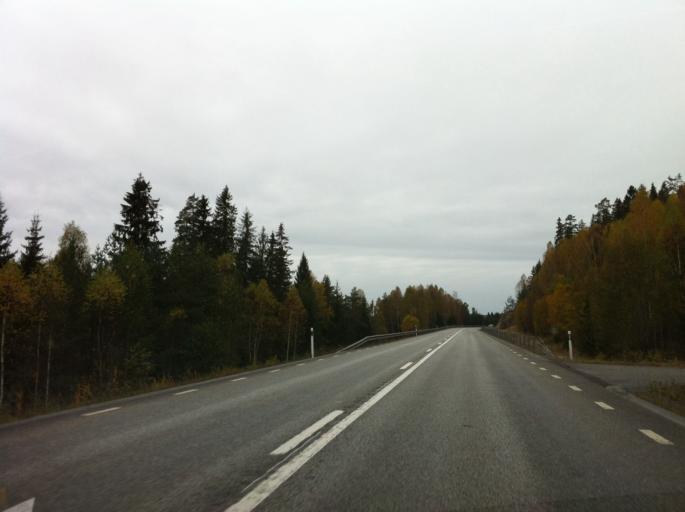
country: SE
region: OErebro
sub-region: Ljusnarsbergs Kommun
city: Kopparberg
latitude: 59.8503
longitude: 15.0646
